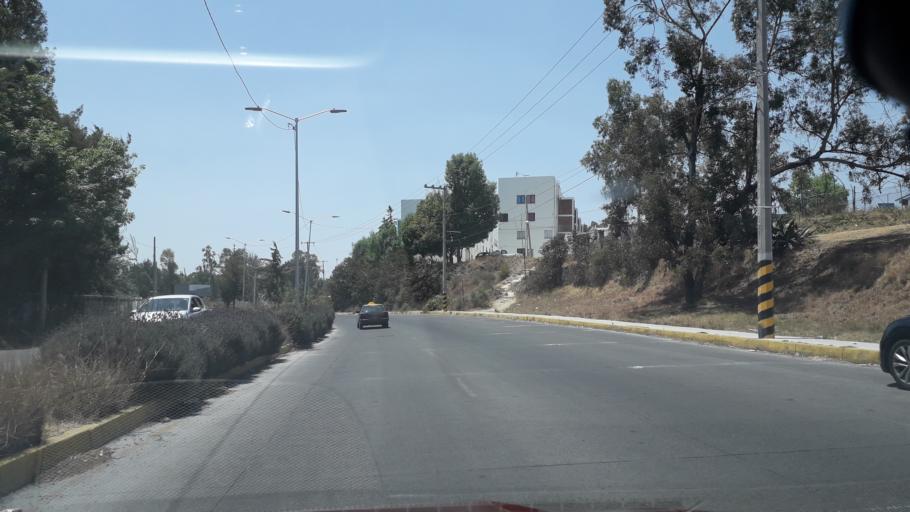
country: MX
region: Puebla
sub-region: Puebla
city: Galaxia la Calera
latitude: 19.0066
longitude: -98.1834
